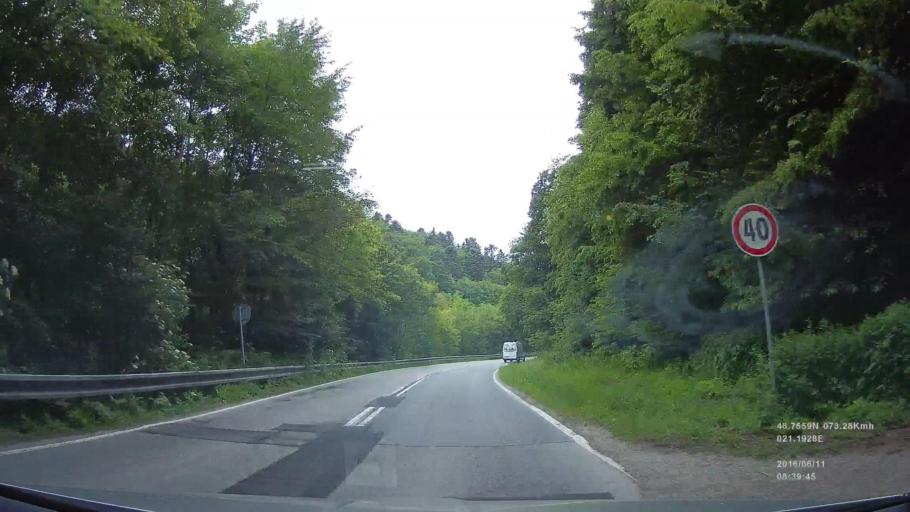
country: SK
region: Kosicky
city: Kosice
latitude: 48.7441
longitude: 21.2374
